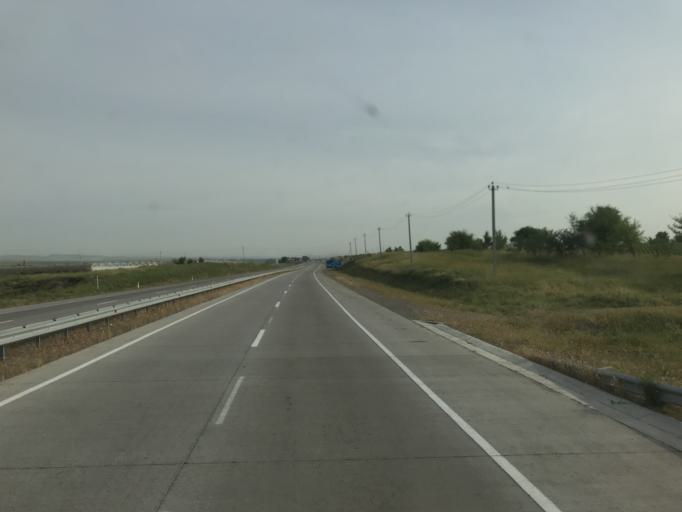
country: KZ
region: Ongtustik Qazaqstan
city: Qazyqurt
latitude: 41.6800
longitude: 69.3936
